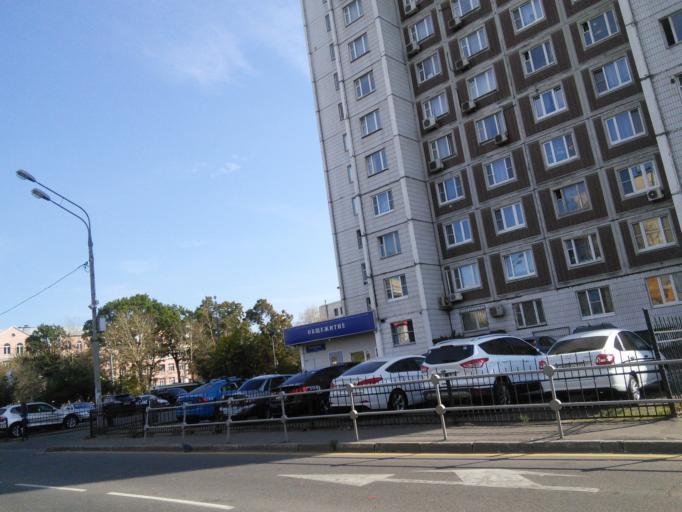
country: RU
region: Moscow
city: Mar'ina Roshcha
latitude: 55.8055
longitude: 37.5811
